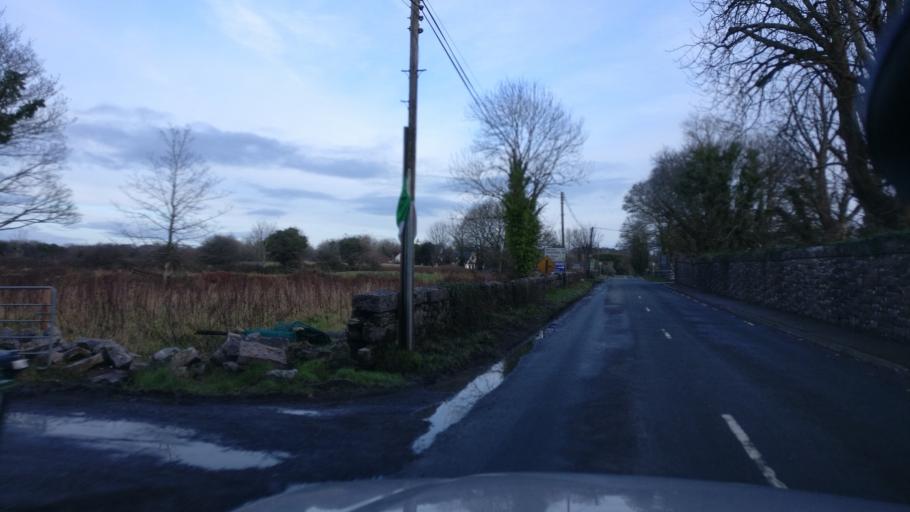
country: IE
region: Connaught
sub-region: Maigh Eo
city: Ballinrobe
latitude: 53.5420
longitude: -9.2716
